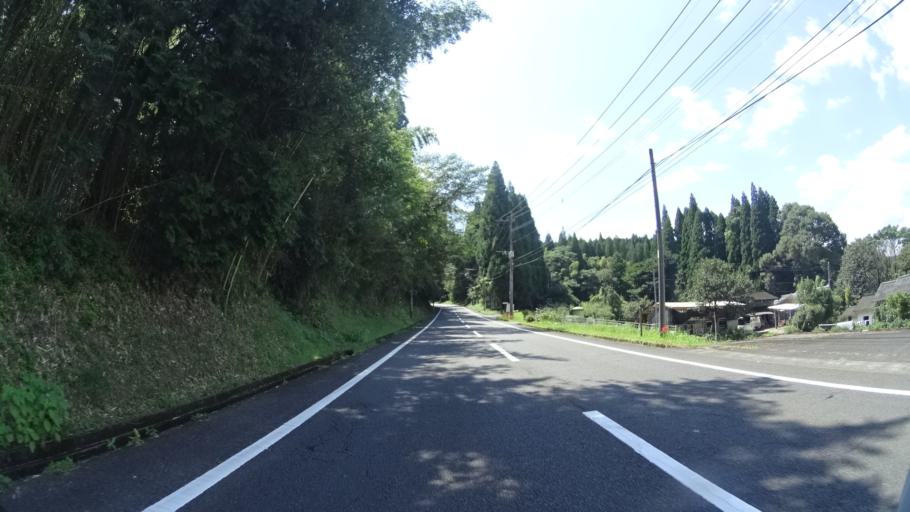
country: JP
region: Kagoshima
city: Kokubu-matsuki
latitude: 31.8251
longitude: 130.7238
